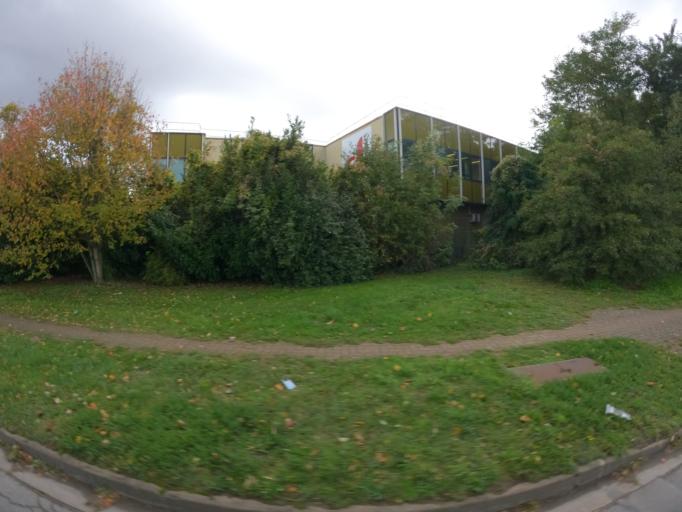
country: FR
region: Ile-de-France
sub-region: Departement de Seine-et-Marne
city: Emerainville
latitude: 48.8178
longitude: 2.6158
